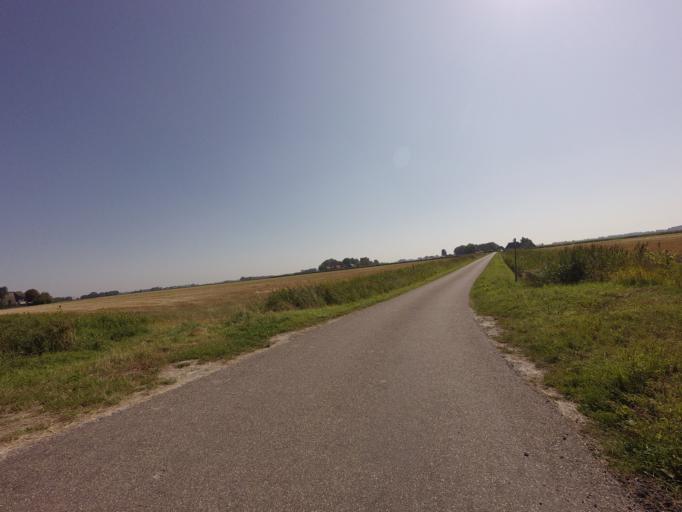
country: NL
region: Friesland
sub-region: Gemeente Dongeradeel
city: Holwerd
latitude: 53.3697
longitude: 5.9190
